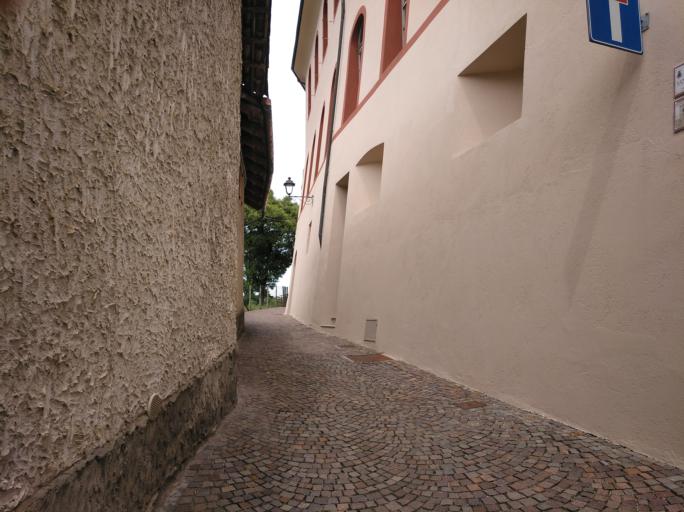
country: IT
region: Piedmont
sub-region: Provincia di Cuneo
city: Barolo
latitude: 44.6111
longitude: 7.9437
